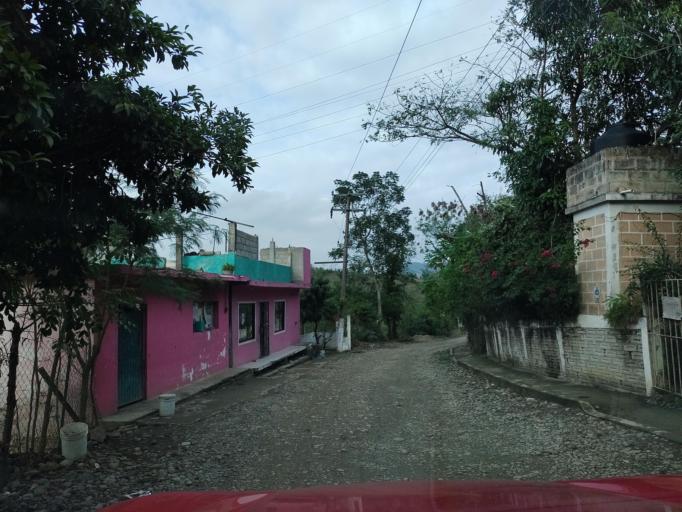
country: MX
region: Veracruz
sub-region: Papantla
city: El Chote
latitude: 20.4415
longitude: -97.4065
